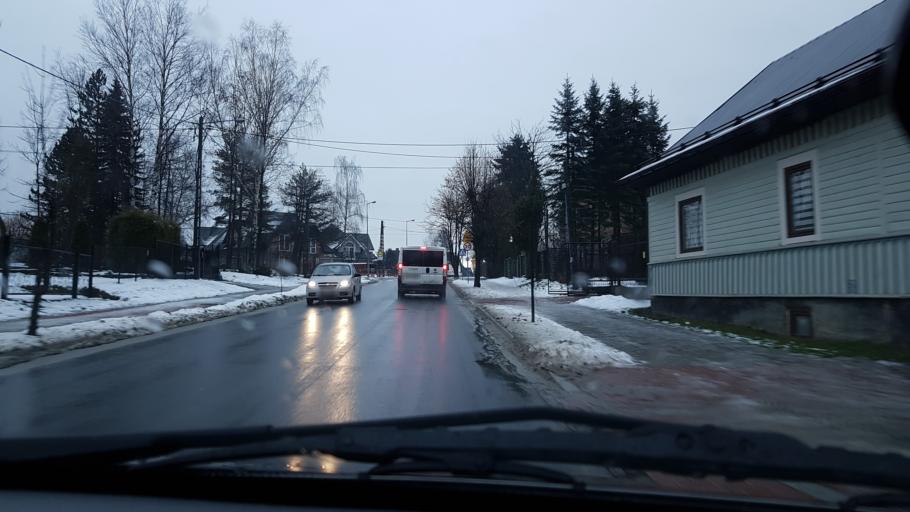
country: PL
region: Lesser Poland Voivodeship
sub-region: Powiat nowotarski
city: Nowy Targ
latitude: 49.4779
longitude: 20.0486
